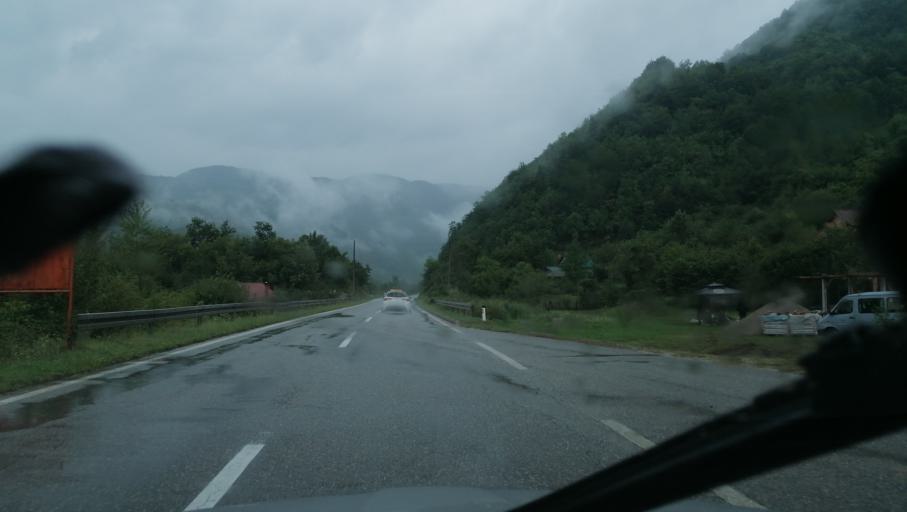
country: BA
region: Republika Srpska
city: Visegrad
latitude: 43.7137
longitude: 19.1685
